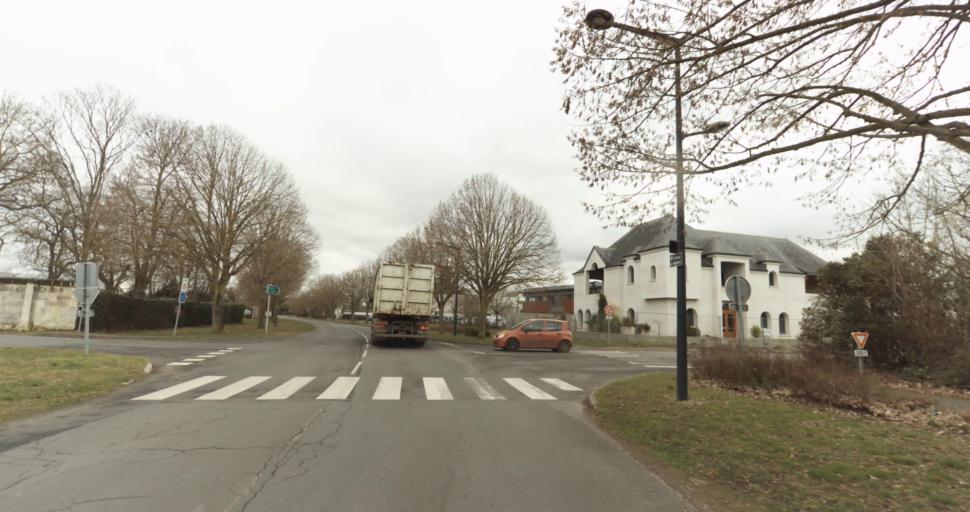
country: FR
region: Pays de la Loire
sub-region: Departement de Maine-et-Loire
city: Saumur
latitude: 47.2735
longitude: -0.0697
